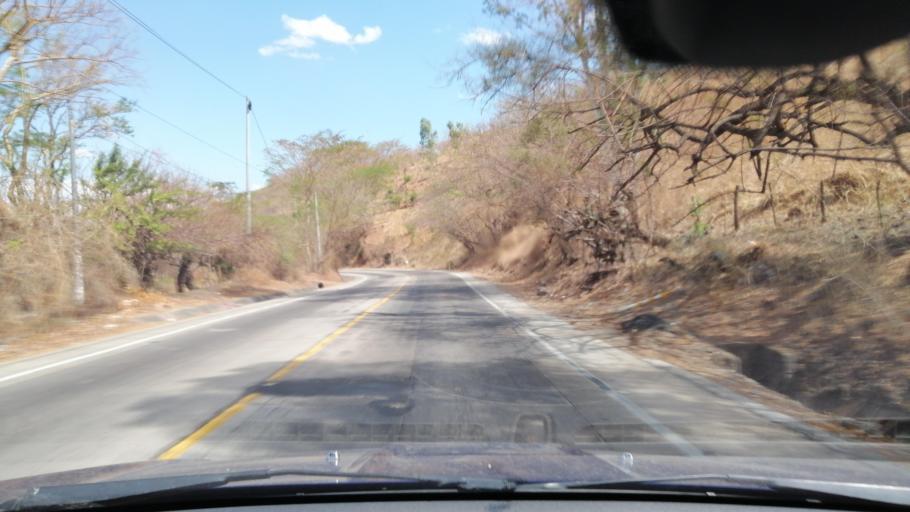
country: SV
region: Santa Ana
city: Texistepeque
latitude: 14.1868
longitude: -89.4942
